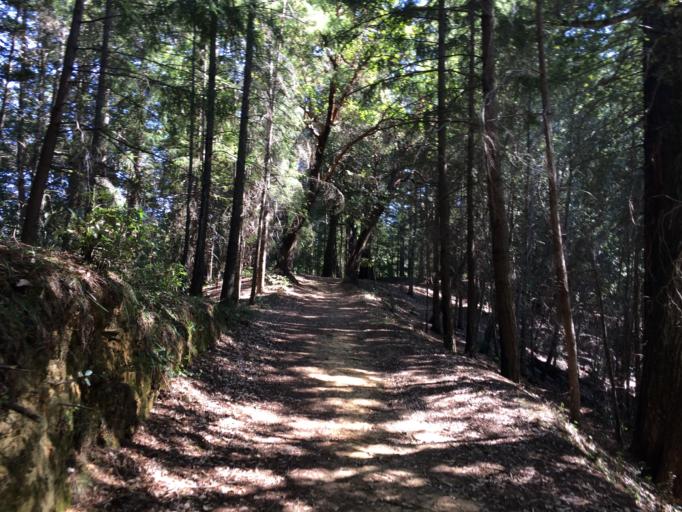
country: US
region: California
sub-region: Santa Cruz County
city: Boulder Creek
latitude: 37.1953
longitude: -122.2318
